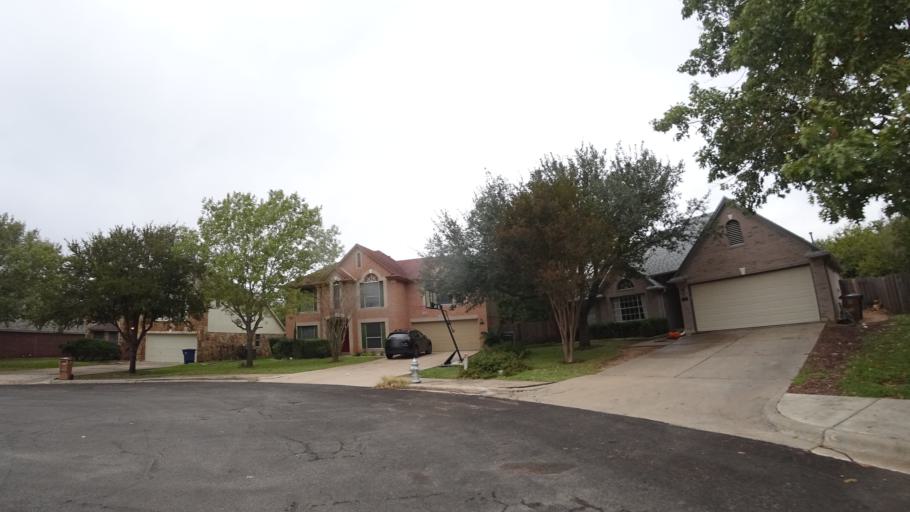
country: US
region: Texas
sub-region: Travis County
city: Shady Hollow
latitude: 30.1906
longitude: -97.8433
